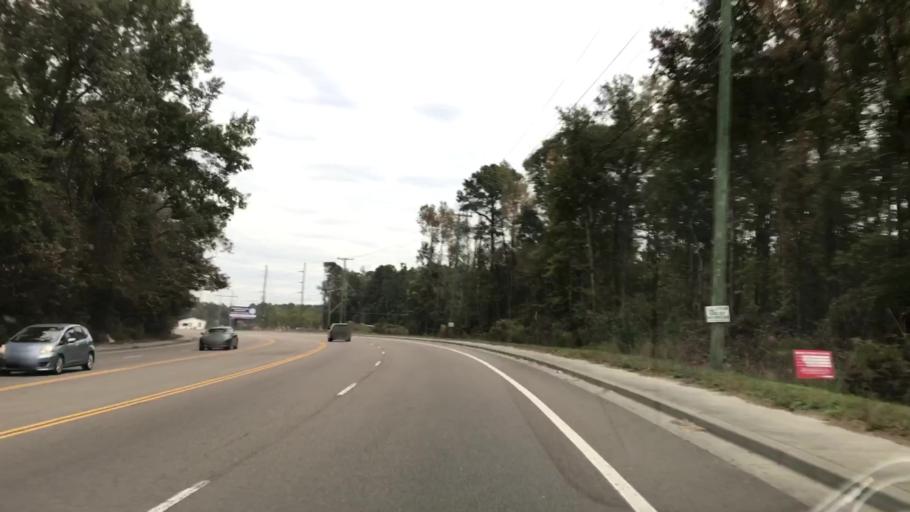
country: US
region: South Carolina
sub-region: Berkeley County
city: Ladson
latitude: 33.0033
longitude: -80.0883
